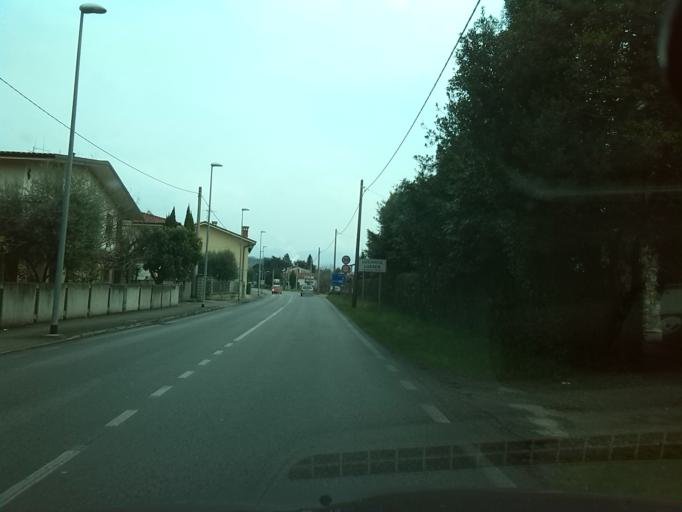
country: IT
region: Friuli Venezia Giulia
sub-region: Provincia di Gorizia
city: Mossa
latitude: 45.9351
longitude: 13.5519
